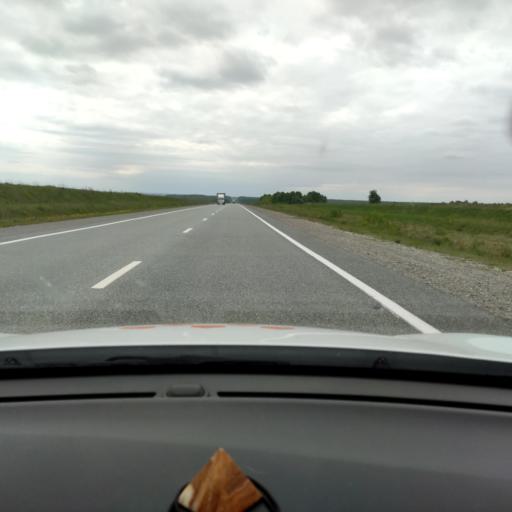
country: RU
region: Tatarstan
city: Pestretsy
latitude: 55.6255
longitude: 49.6937
